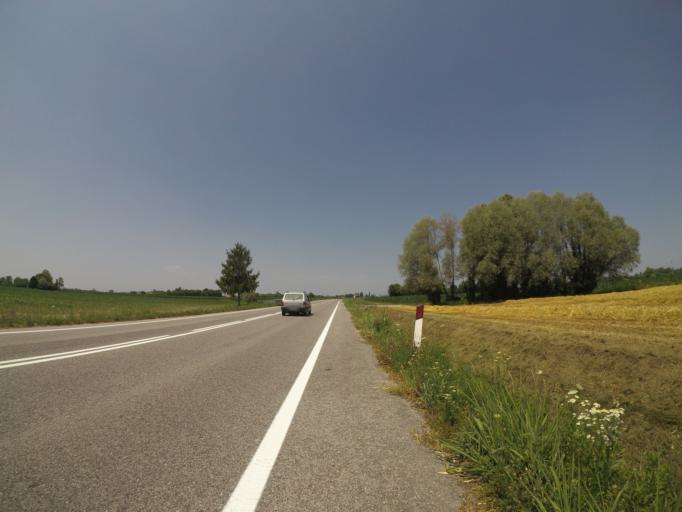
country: IT
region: Friuli Venezia Giulia
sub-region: Provincia di Udine
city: Varmo
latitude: 45.8972
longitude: 13.0076
